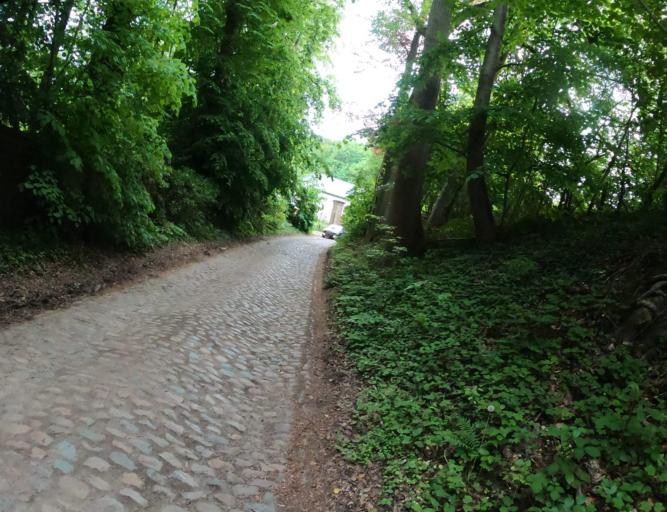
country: BE
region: Flanders
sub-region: Provincie Vlaams-Brabant
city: Sint-Genesius-Rode
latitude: 50.7194
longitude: 4.3299
